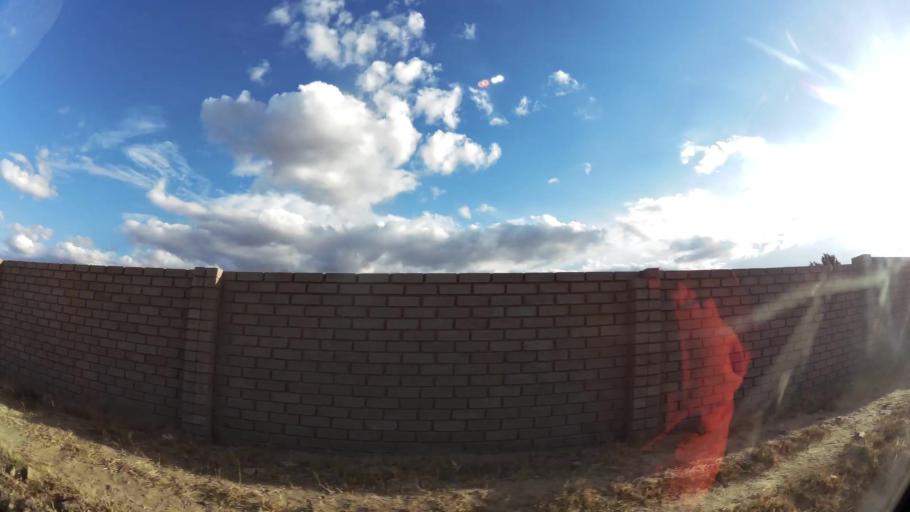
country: ZA
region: Limpopo
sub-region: Capricorn District Municipality
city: Polokwane
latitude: -23.9266
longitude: 29.4372
